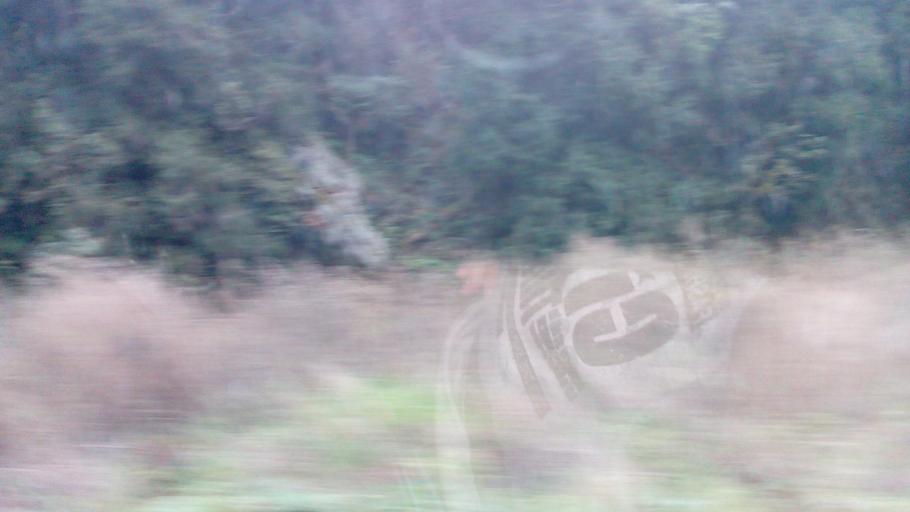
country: TW
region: Taiwan
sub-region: Hualien
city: Hualian
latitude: 24.3950
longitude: 121.3545
